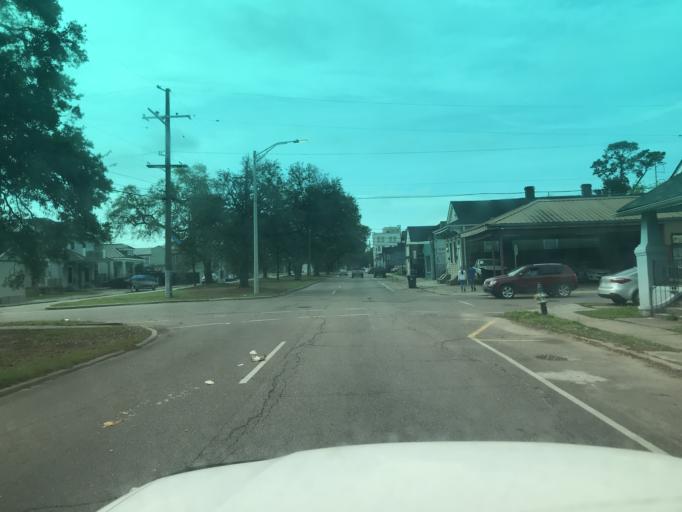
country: US
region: Louisiana
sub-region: Orleans Parish
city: New Orleans
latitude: 29.9785
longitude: -90.0485
